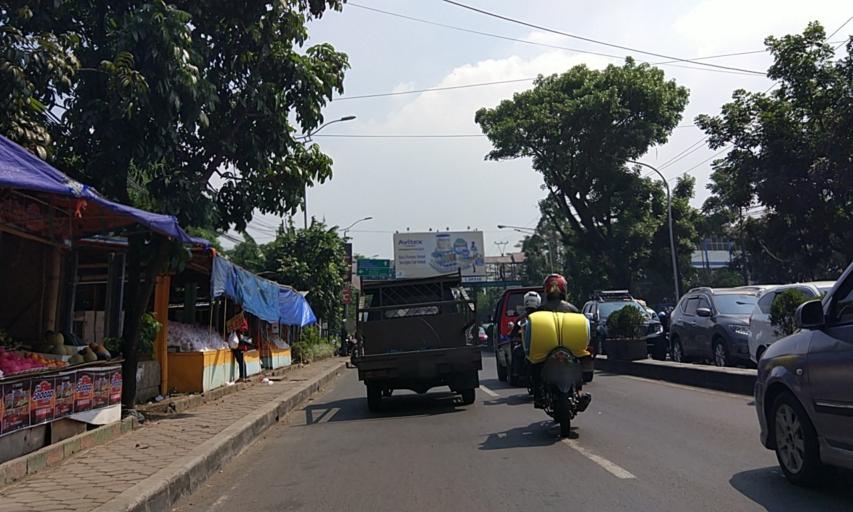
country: ID
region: West Java
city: Cimahi
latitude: -6.9025
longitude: 107.5641
